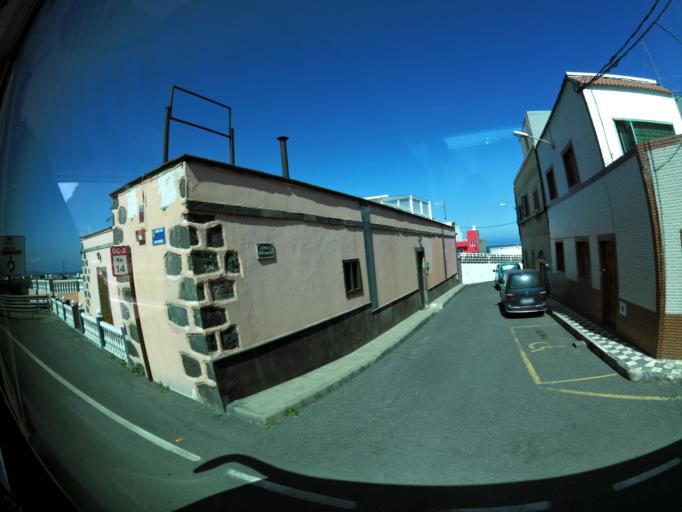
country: ES
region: Canary Islands
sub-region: Provincia de Las Palmas
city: Firgas
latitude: 28.1452
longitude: -15.5583
